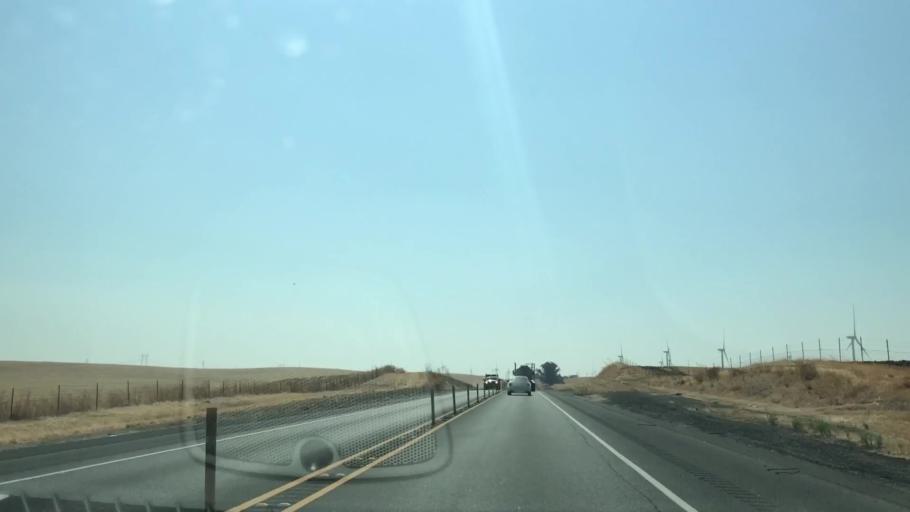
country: US
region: California
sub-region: Solano County
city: Suisun
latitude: 38.2032
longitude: -121.8713
